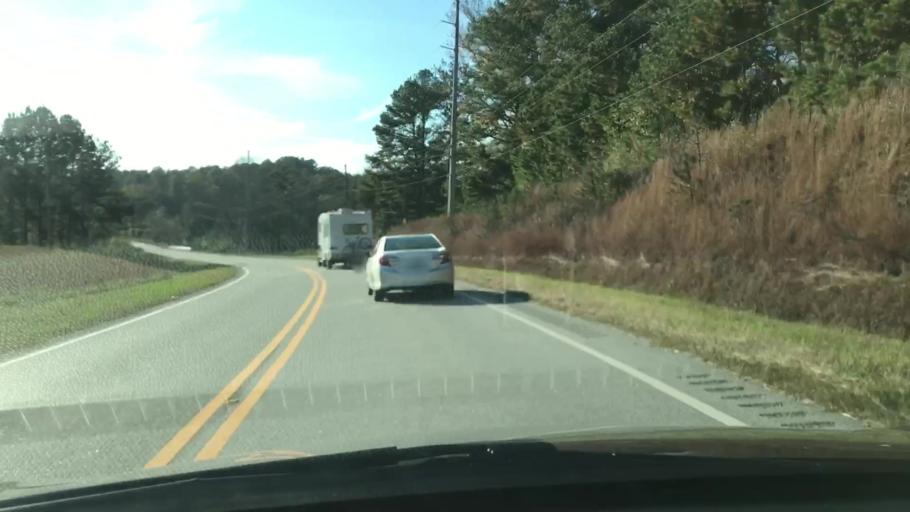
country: US
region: Alabama
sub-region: Cleburne County
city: Heflin
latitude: 33.6545
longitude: -85.5289
